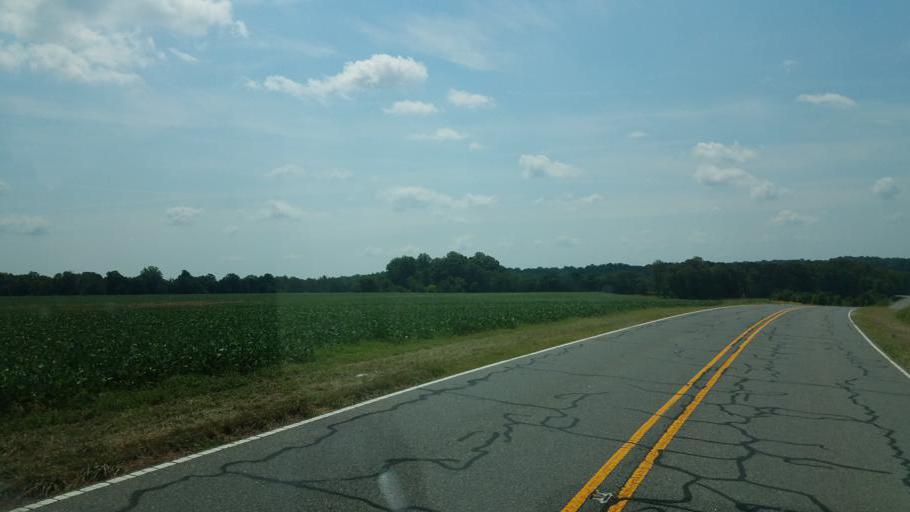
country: US
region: North Carolina
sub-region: Gaston County
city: Cherryville
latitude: 35.4270
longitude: -81.4124
